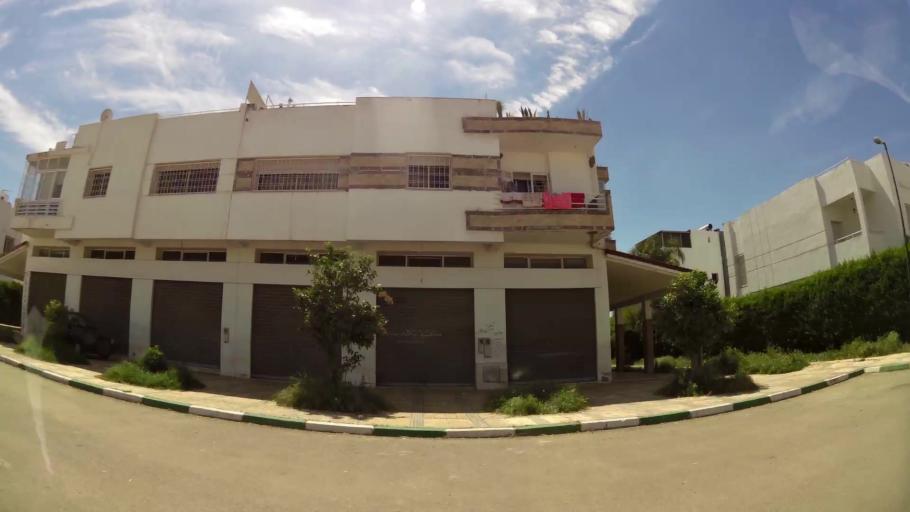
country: MA
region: Fes-Boulemane
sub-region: Fes
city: Fes
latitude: 34.0084
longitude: -4.9911
